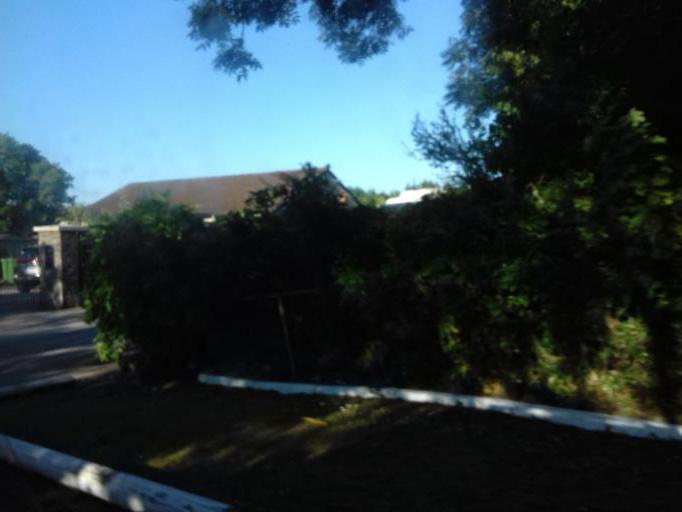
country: IE
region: Leinster
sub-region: An Mhi
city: Ashbourne
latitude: 53.4735
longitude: -6.3393
